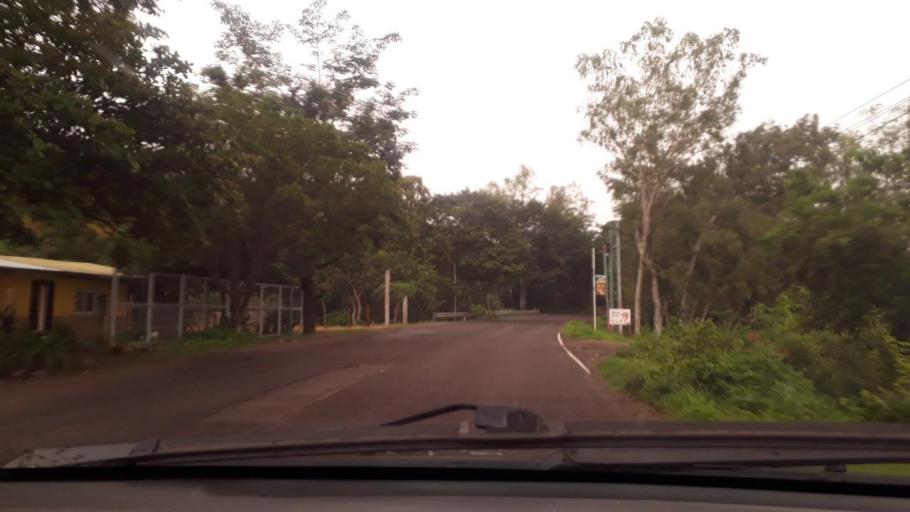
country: GT
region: Jutiapa
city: Jalpatagua
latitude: 14.1151
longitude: -89.9725
